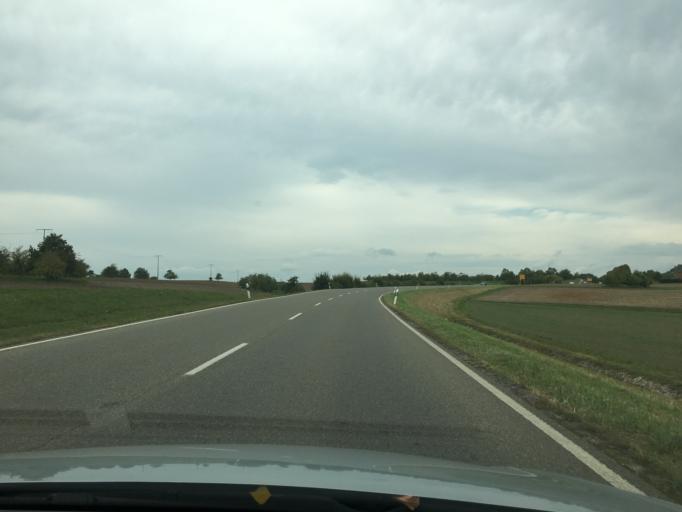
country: DE
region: Baden-Wuerttemberg
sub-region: Regierungsbezirk Stuttgart
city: Hildrizhausen
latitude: 48.5685
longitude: 8.9403
